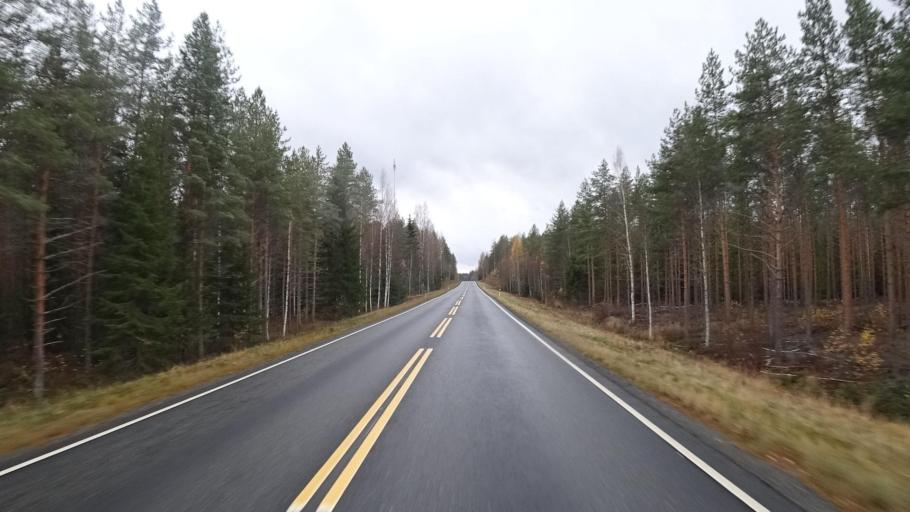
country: FI
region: Southern Savonia
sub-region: Mikkeli
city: Kangasniemi
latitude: 62.1528
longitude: 26.8160
